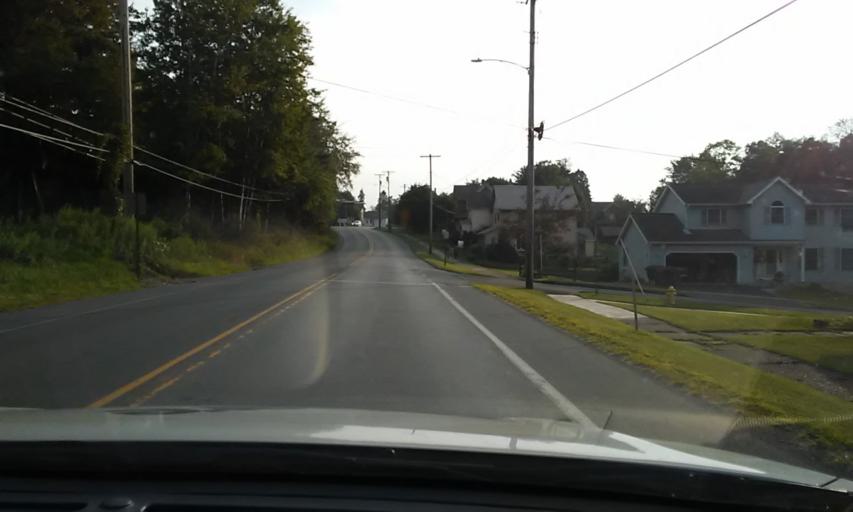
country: US
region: Pennsylvania
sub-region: McKean County
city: Kane
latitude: 41.6615
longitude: -78.7962
